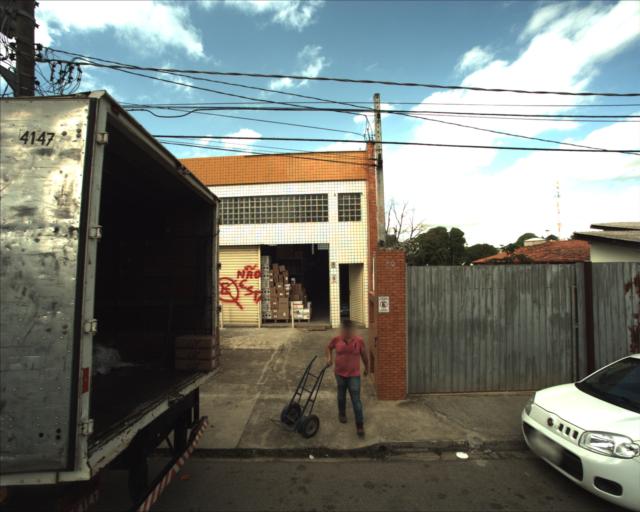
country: BR
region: Sao Paulo
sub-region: Sorocaba
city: Sorocaba
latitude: -23.3983
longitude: -47.3770
